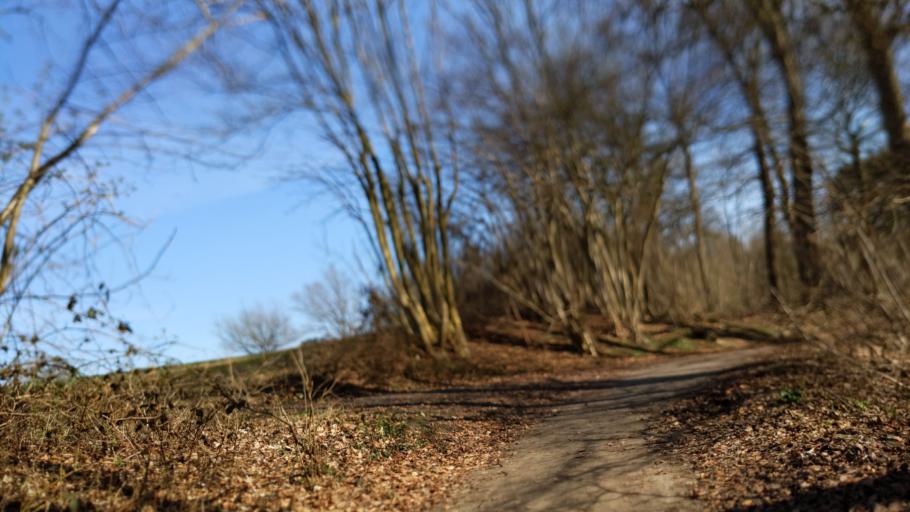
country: DE
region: Schleswig-Holstein
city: Travemuende
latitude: 53.9843
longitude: 10.8256
